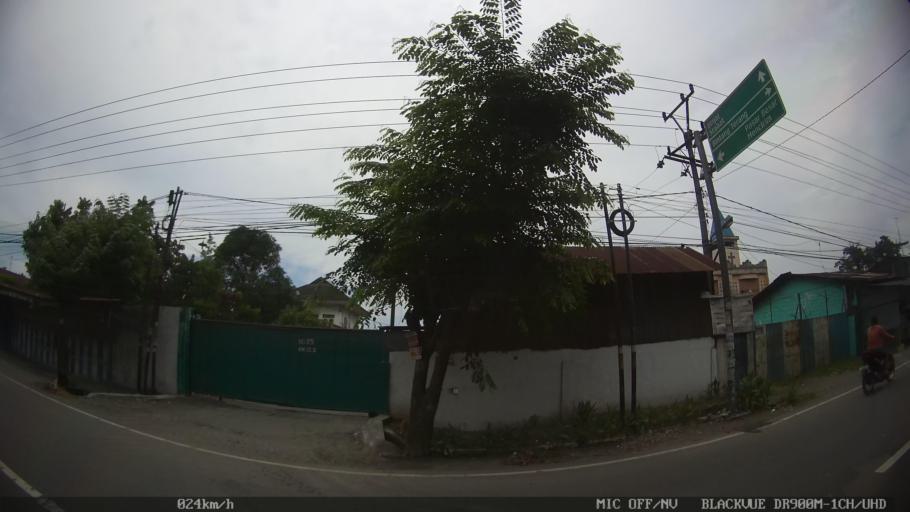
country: ID
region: North Sumatra
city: Sunggal
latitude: 3.5990
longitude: 98.5655
